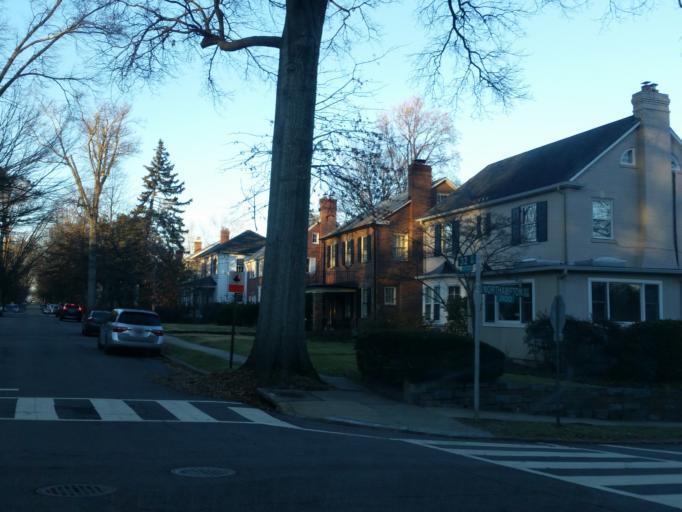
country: US
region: Maryland
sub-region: Montgomery County
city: Chevy Chase
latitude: 38.9658
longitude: -77.0639
